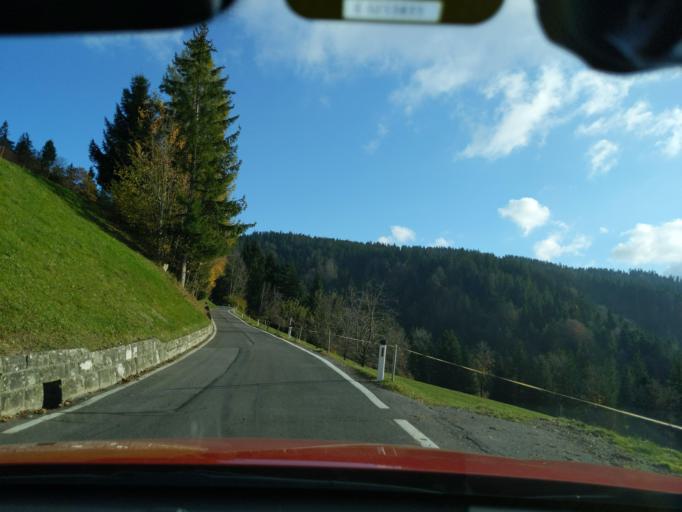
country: AT
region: Vorarlberg
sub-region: Politischer Bezirk Bregenz
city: Eichenberg
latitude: 47.5441
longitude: 9.7913
